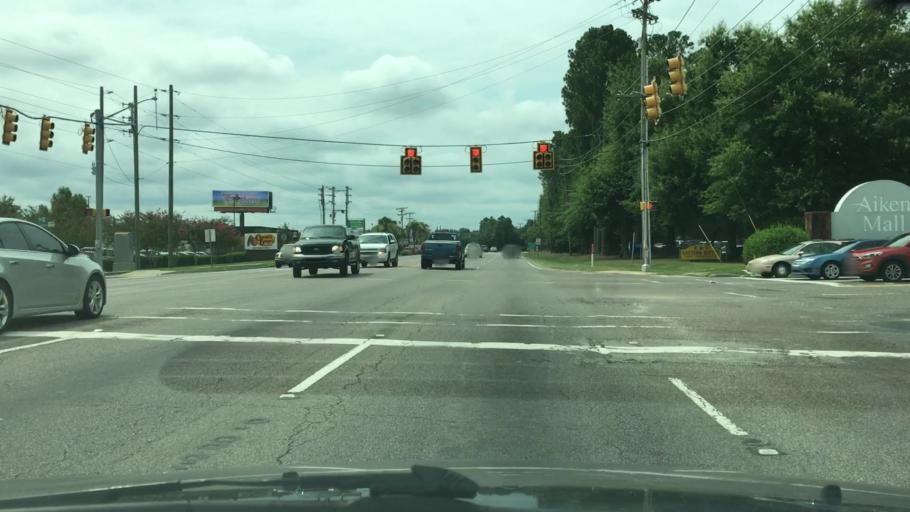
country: US
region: South Carolina
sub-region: Aiken County
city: Aiken
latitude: 33.5115
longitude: -81.7133
